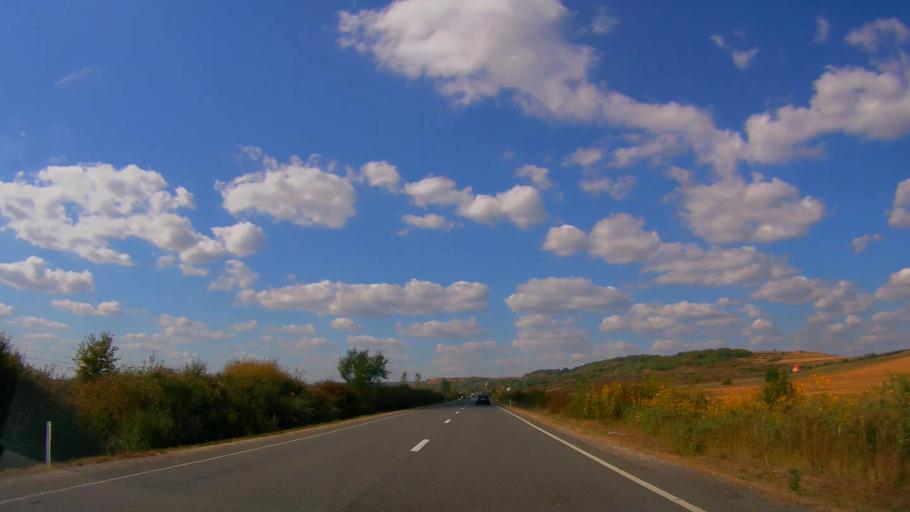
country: RO
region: Salaj
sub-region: Comuna Bocsa
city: Bocsa
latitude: 47.3082
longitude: 22.9193
